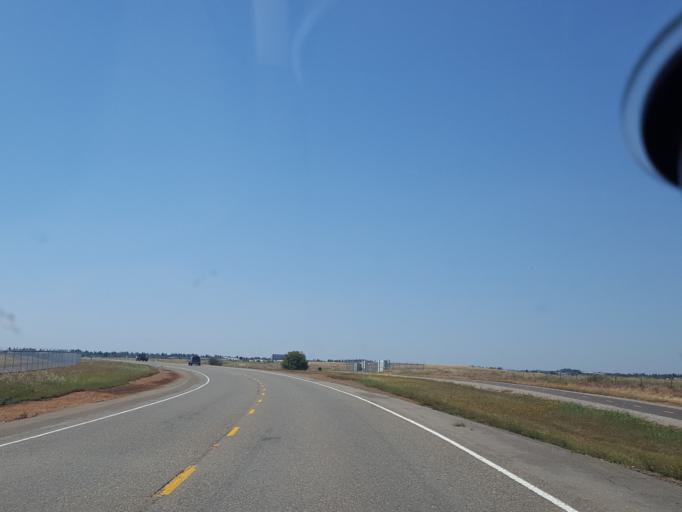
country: US
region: California
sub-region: Sacramento County
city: Rancho Cordova
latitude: 38.5638
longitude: -121.2679
